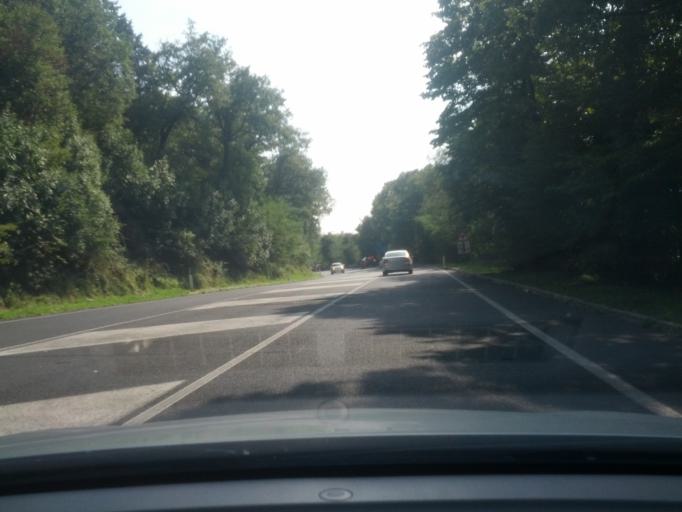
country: IT
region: Friuli Venezia Giulia
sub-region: Provincia di Trieste
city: Villa Opicina
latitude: 45.6700
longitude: 13.7917
